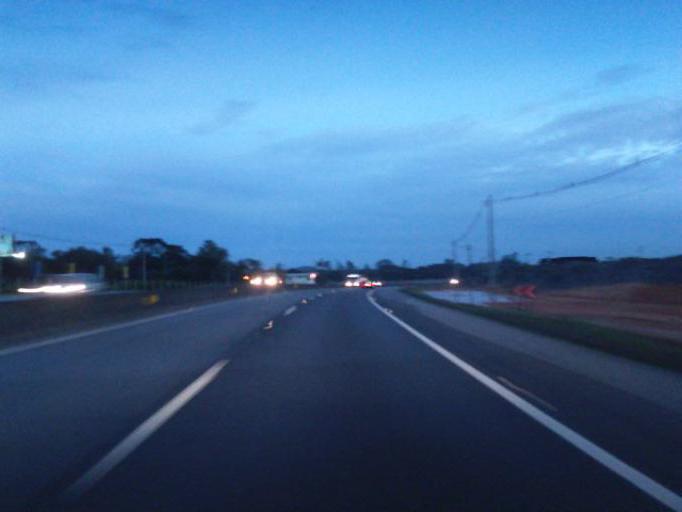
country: BR
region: Santa Catarina
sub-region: Barra Velha
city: Barra Velha
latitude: -26.4638
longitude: -48.7513
